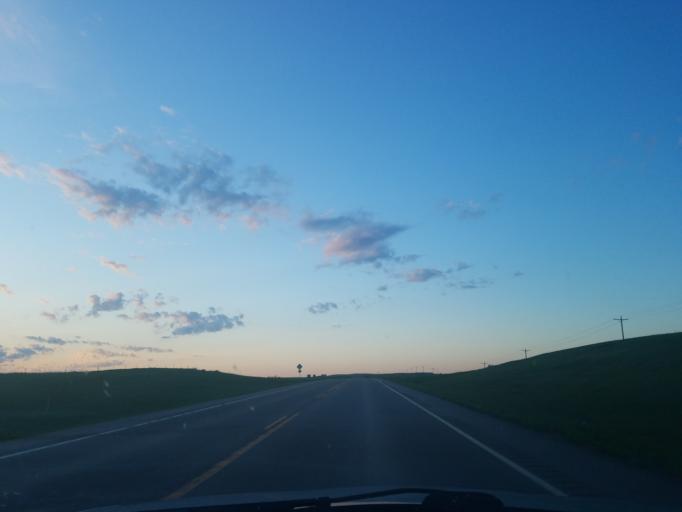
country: US
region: North Dakota
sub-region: McKenzie County
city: Watford City
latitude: 47.6238
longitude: -103.2695
